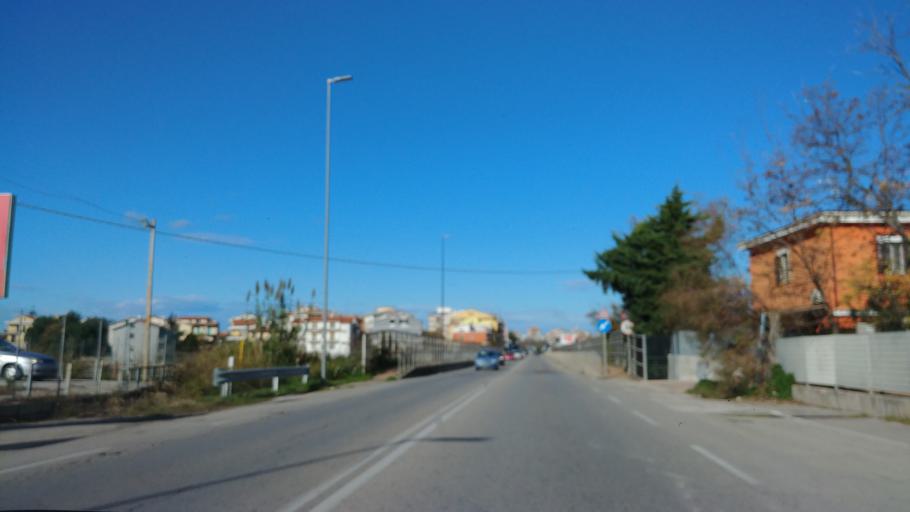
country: IT
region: Molise
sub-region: Provincia di Campobasso
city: Termoli
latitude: 41.9895
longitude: 15.0011
